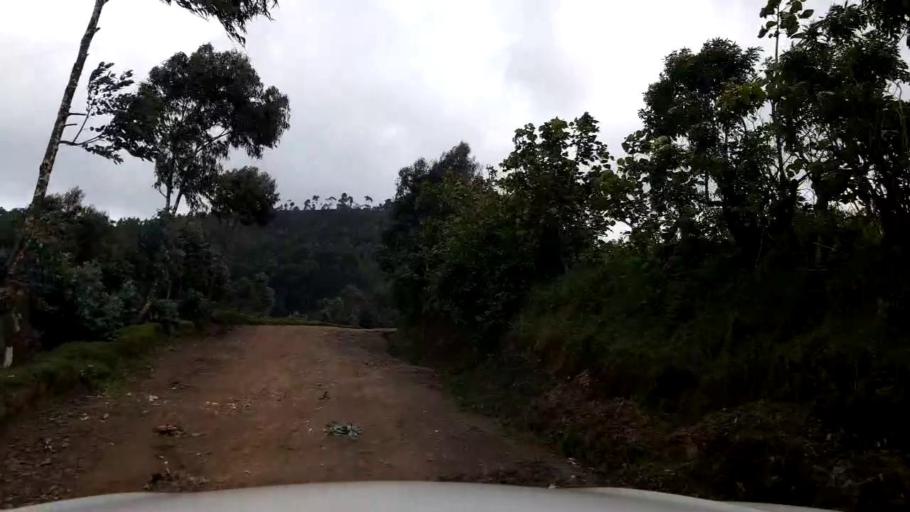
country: RW
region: Western Province
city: Kibuye
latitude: -1.9543
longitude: 29.4744
